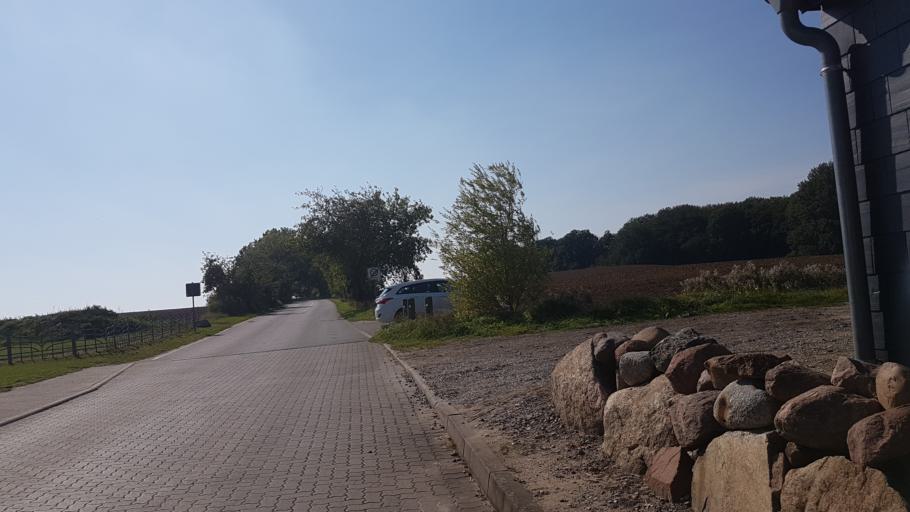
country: DE
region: Mecklenburg-Vorpommern
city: Putbus
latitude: 54.3540
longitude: 13.5123
